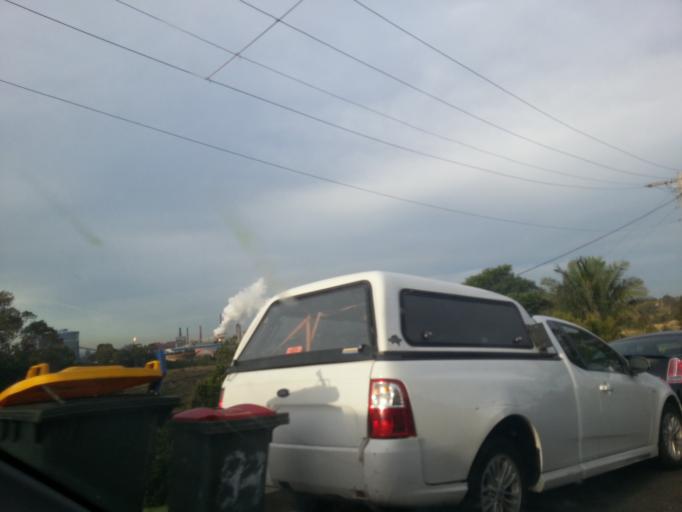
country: AU
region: New South Wales
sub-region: Wollongong
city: Lake Heights
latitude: -34.4764
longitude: 150.8734
